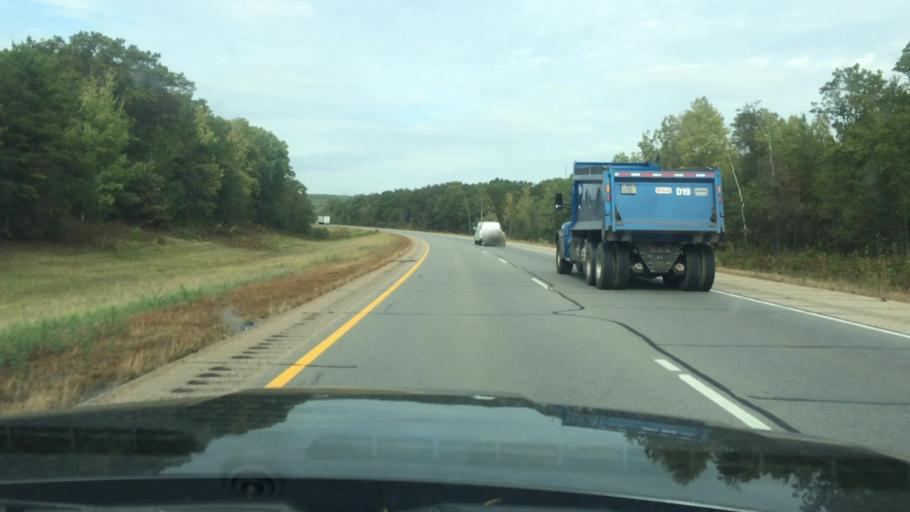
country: US
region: Wisconsin
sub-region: Marathon County
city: Mosinee
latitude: 44.6898
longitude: -89.6410
